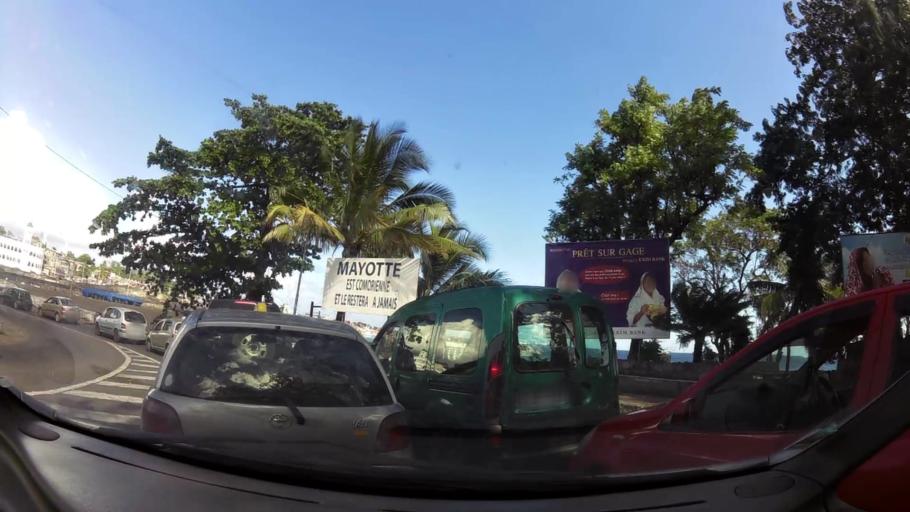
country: KM
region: Grande Comore
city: Moroni
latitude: -11.7017
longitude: 43.2518
